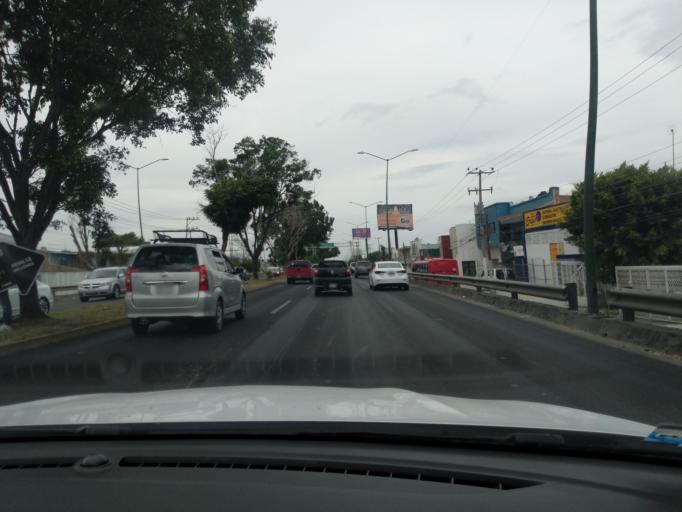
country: MX
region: Jalisco
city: Nuevo Mexico
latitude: 20.7658
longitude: -103.4411
